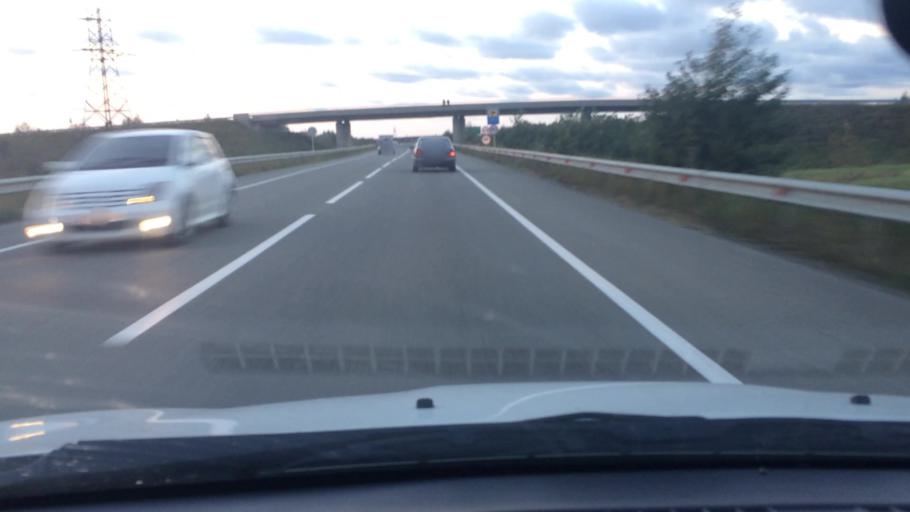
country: GE
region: Ajaria
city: Ochkhamuri
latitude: 41.8914
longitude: 41.8062
